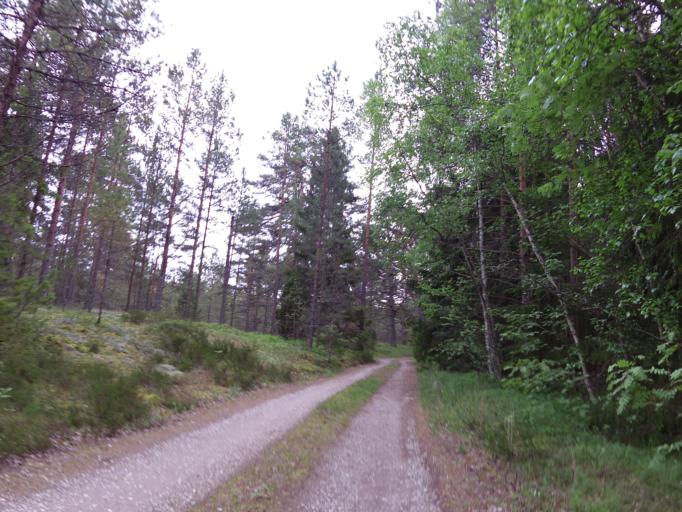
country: EE
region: Harju
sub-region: Paldiski linn
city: Paldiski
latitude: 59.2466
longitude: 23.7477
